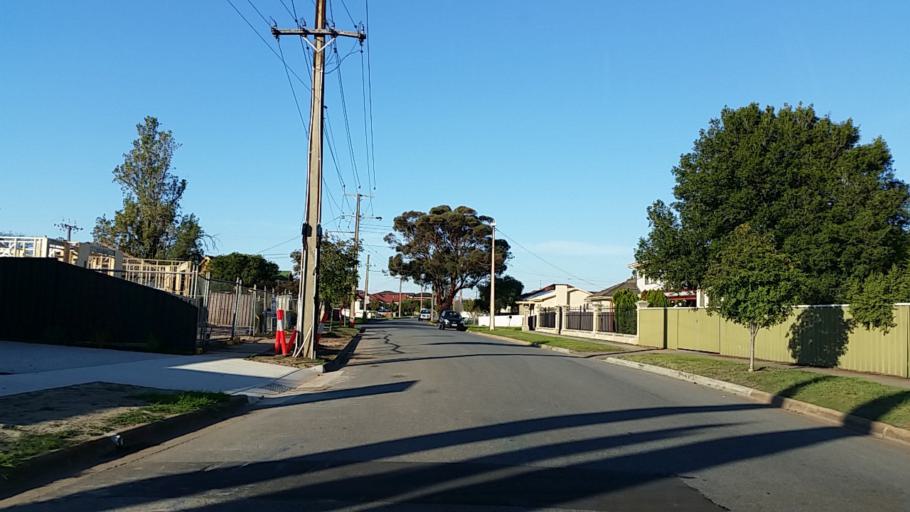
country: AU
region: South Australia
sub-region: Charles Sturt
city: Woodville West
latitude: -34.8898
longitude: 138.5280
